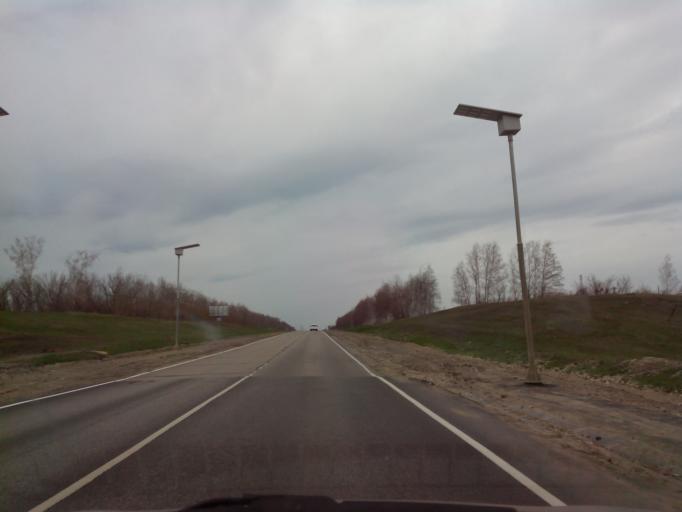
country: RU
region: Tambov
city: Znamenka
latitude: 52.3964
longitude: 41.3968
